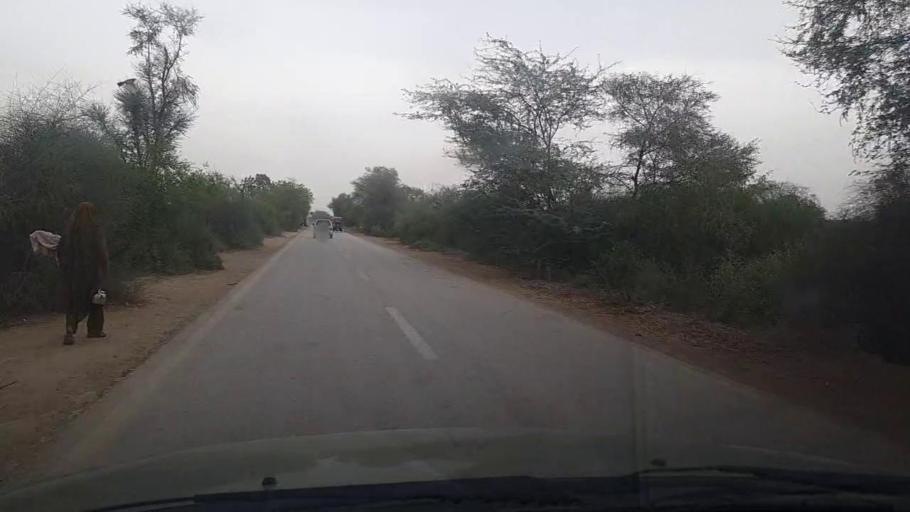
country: PK
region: Sindh
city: Daulatpur
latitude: 26.3287
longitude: 68.1119
